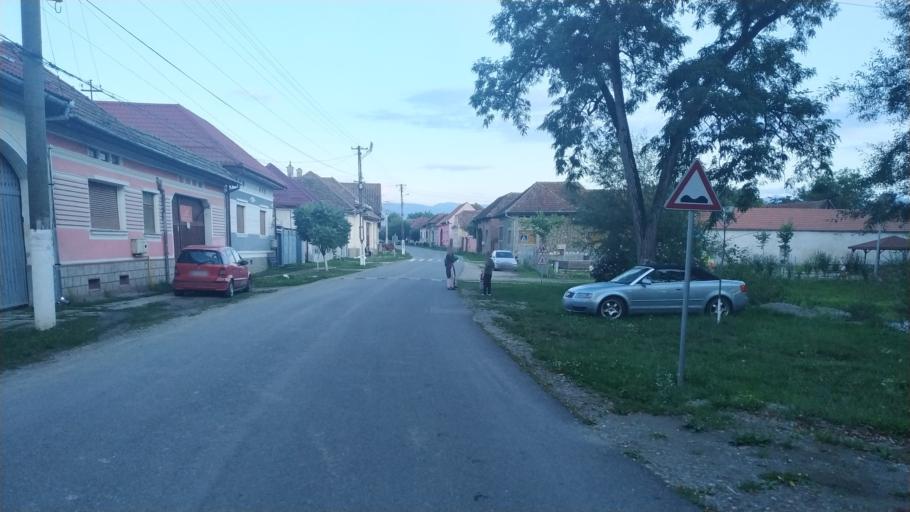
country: RO
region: Brasov
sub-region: Comuna Beclean
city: Beclean
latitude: 45.8299
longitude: 24.9247
